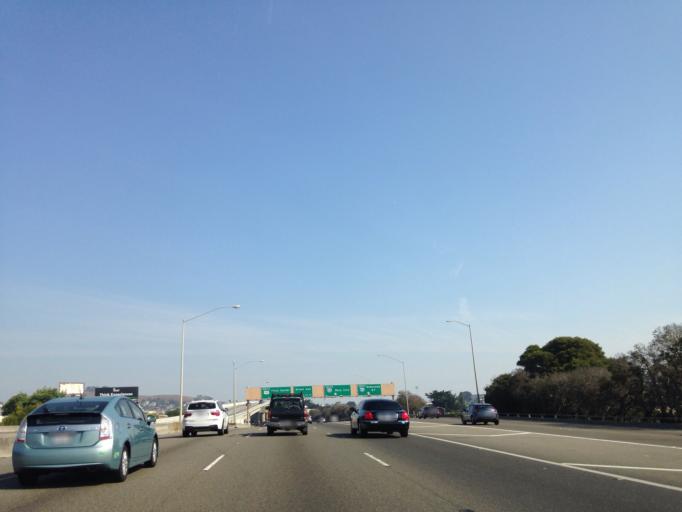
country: US
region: California
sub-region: San Mateo County
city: Brisbane
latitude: 37.7270
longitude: -122.4023
